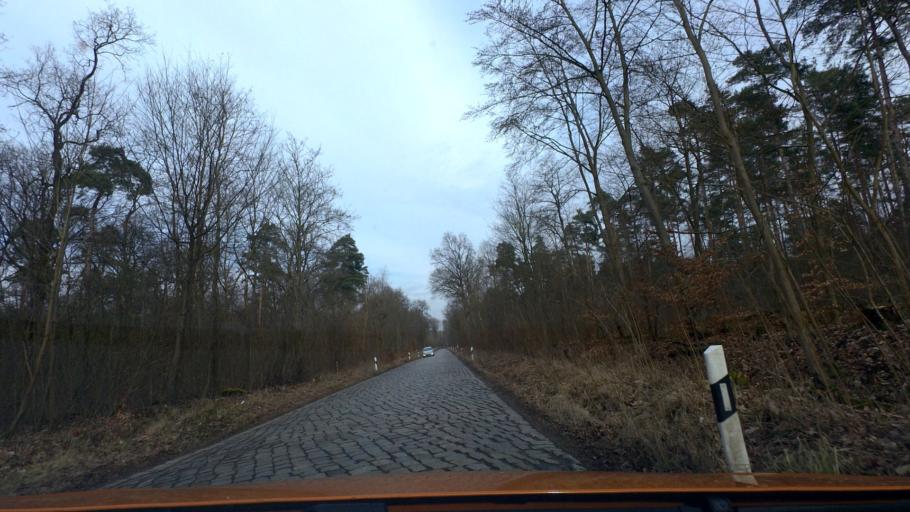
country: DE
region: Berlin
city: Buch
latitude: 52.6534
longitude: 13.4862
